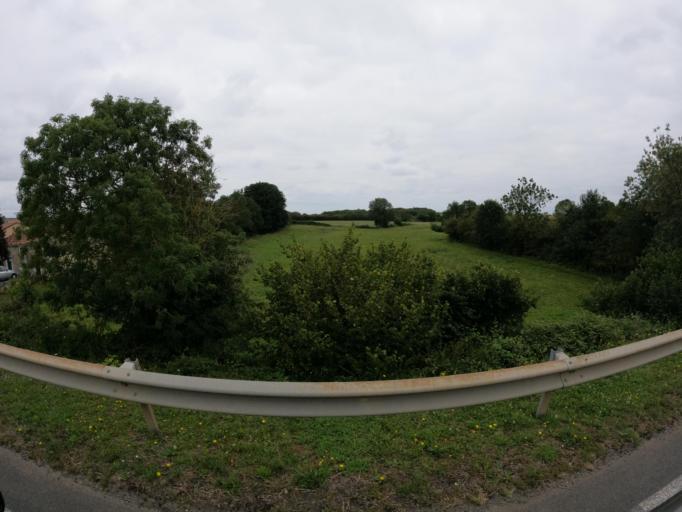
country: FR
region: Pays de la Loire
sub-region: Departement de la Vendee
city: Saint-Hilaire-des-Loges
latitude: 46.4033
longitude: -0.6723
